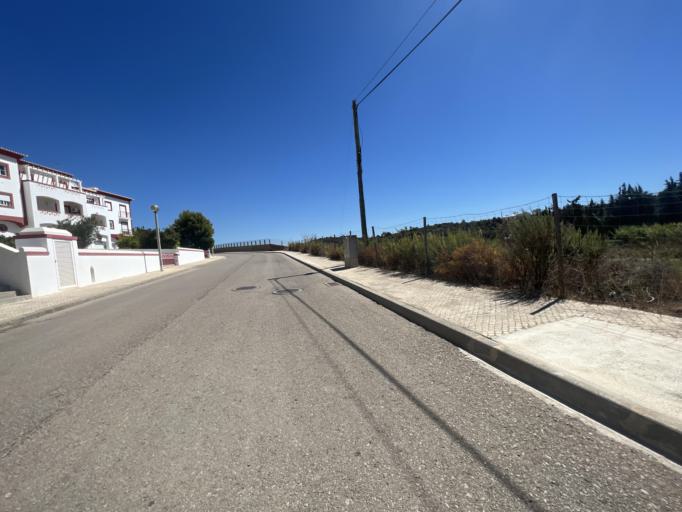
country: PT
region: Faro
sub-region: Portimao
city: Portimao
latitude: 37.1260
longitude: -8.5130
